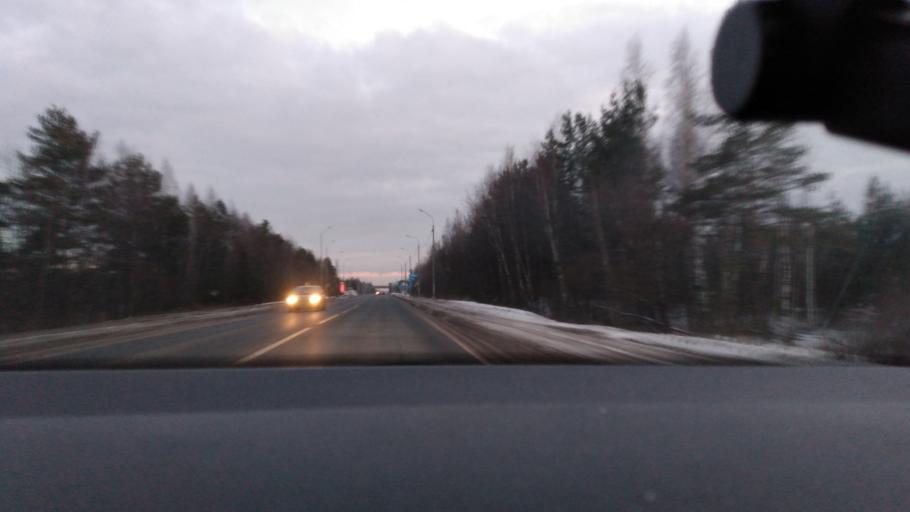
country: RU
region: Moskovskaya
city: Yegor'yevsk
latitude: 55.4208
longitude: 39.0403
